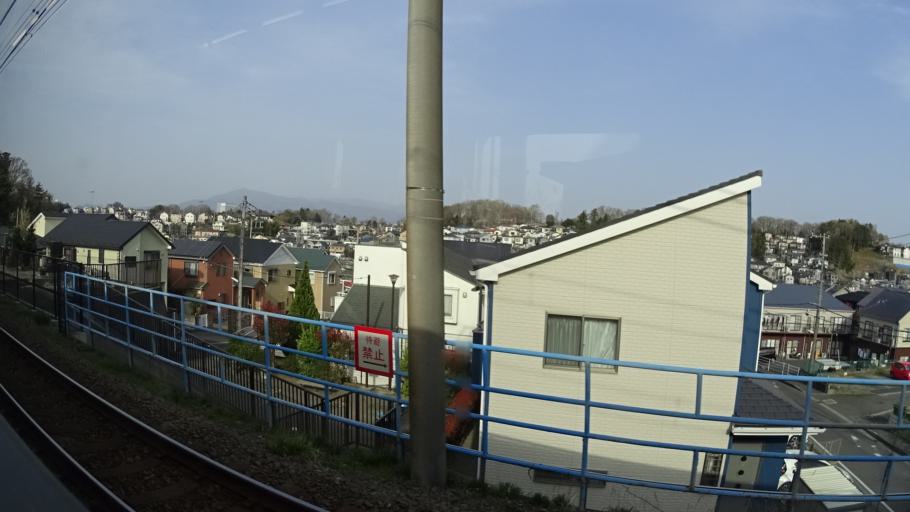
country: JP
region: Kanagawa
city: Zama
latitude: 35.4622
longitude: 139.4093
